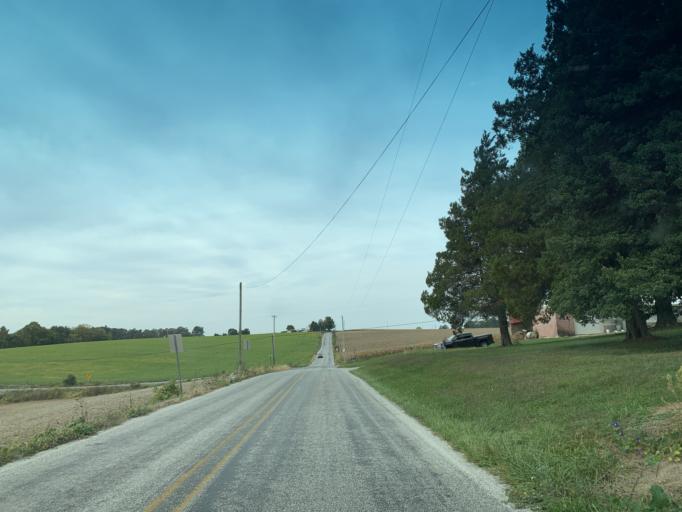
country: US
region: Pennsylvania
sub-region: York County
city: Stewartstown
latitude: 39.8043
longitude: -76.5173
